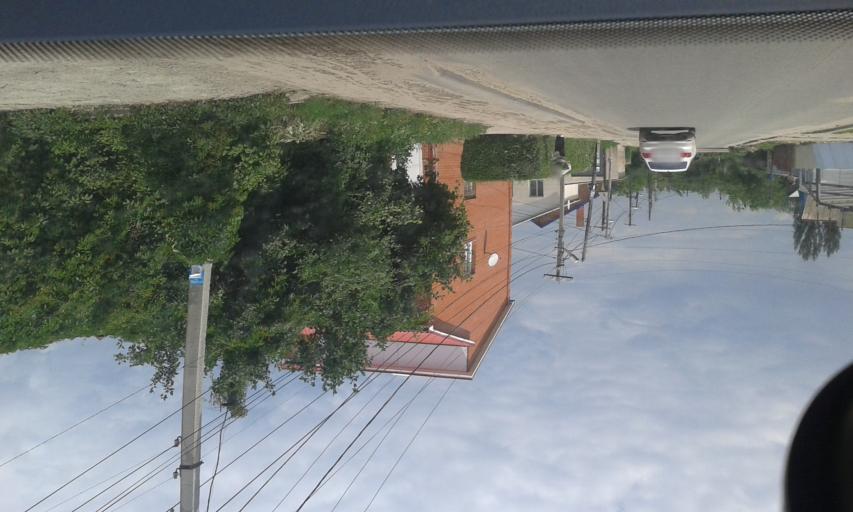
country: RU
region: Volgograd
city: Gorodishche
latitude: 48.7718
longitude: 44.4957
